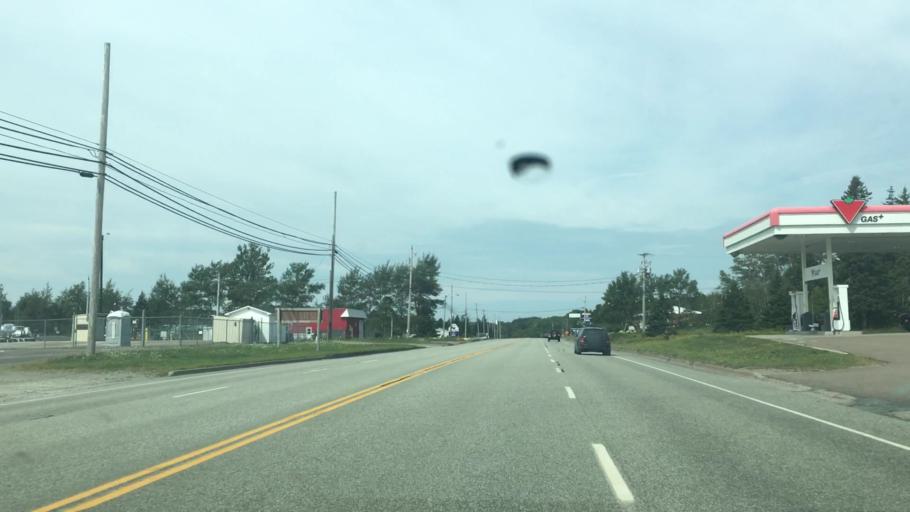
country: CA
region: Nova Scotia
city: Port Hawkesbury
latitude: 45.6404
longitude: -61.3872
